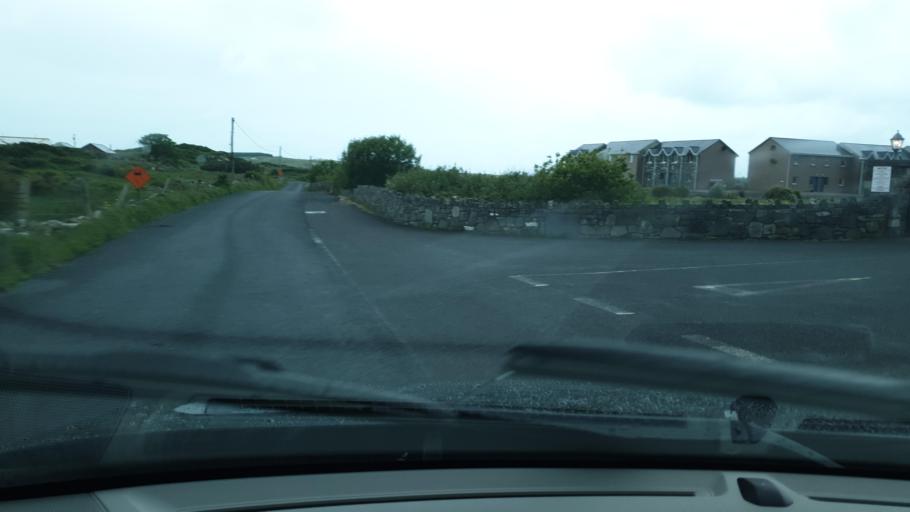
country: IE
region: Connaught
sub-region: County Galway
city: Clifden
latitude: 53.4369
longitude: -10.0776
